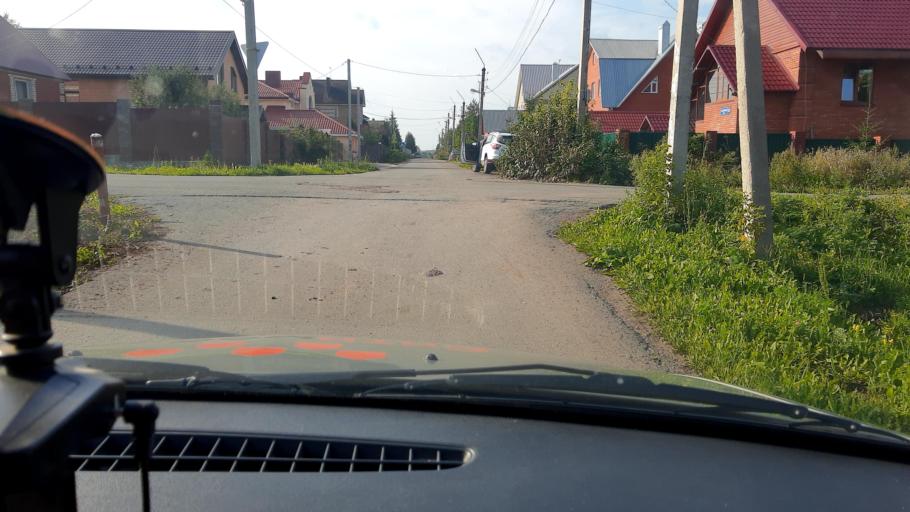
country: RU
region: Bashkortostan
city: Ufa
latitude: 54.5974
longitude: 55.9310
